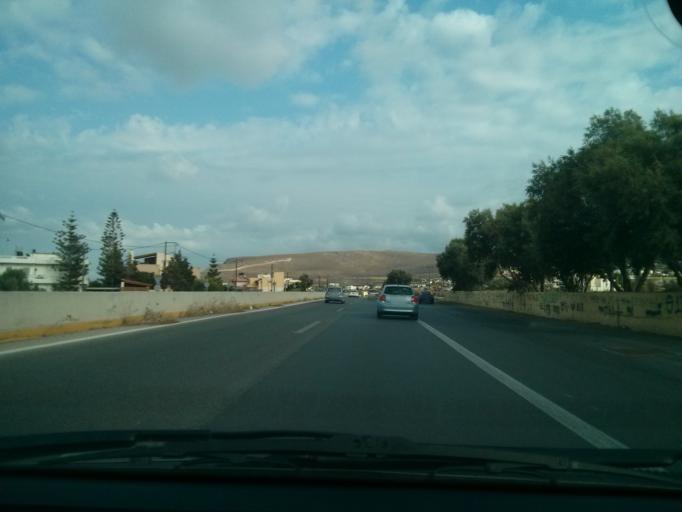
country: GR
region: Crete
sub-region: Nomos Irakleiou
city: Kokkini Hani
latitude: 35.3289
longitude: 25.2477
